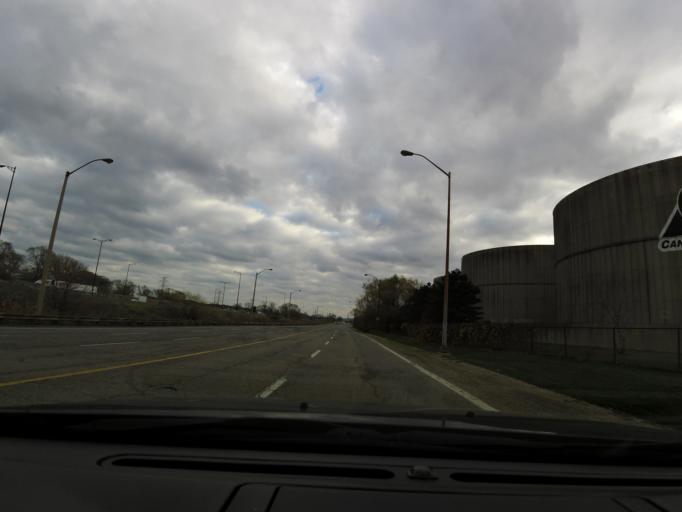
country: CA
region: Ontario
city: Hamilton
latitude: 43.2772
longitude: -79.7862
